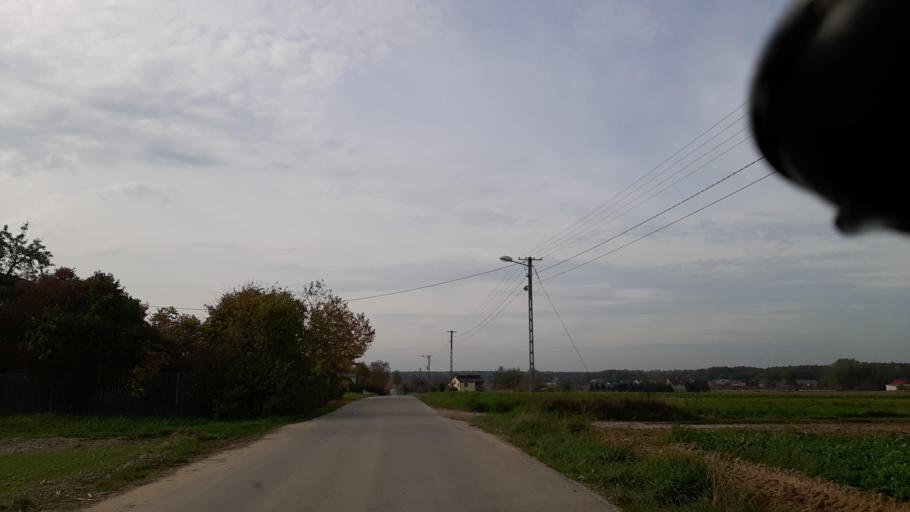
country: PL
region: Lublin Voivodeship
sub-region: Powiat lubelski
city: Garbow
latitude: 51.3912
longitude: 22.3223
